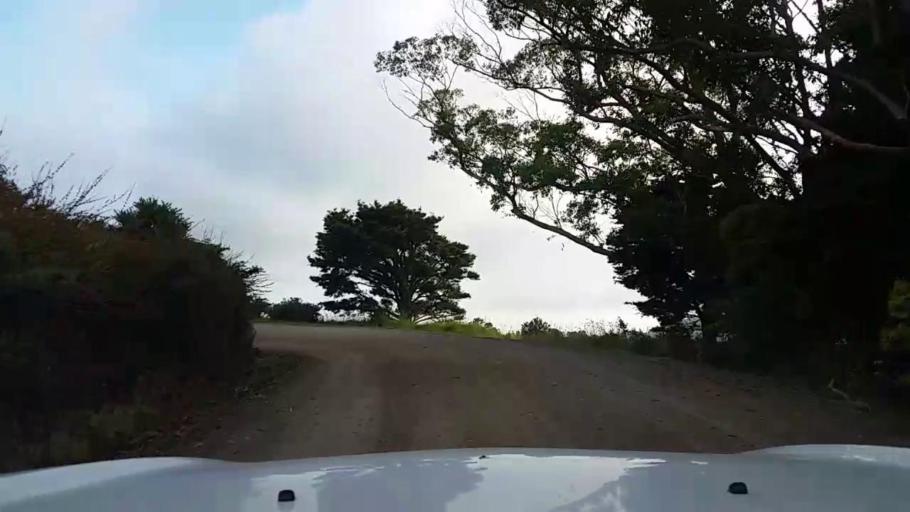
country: NZ
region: Northland
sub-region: Whangarei
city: Maungatapere
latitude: -35.6696
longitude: 174.1757
